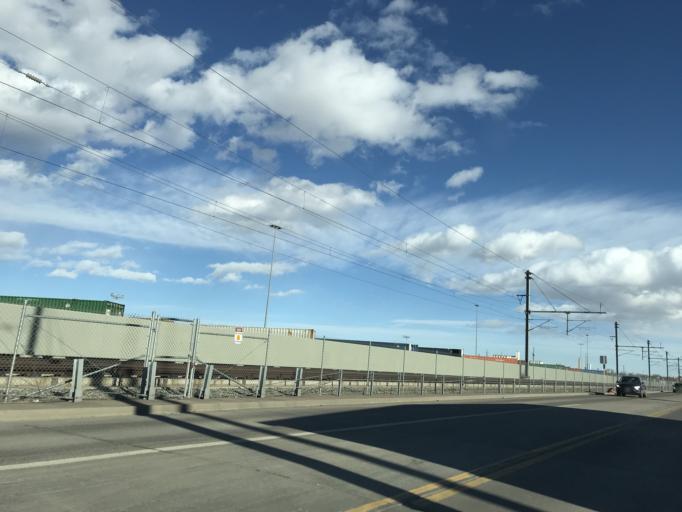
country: US
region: Colorado
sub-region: Denver County
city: Denver
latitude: 39.7729
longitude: -104.9660
